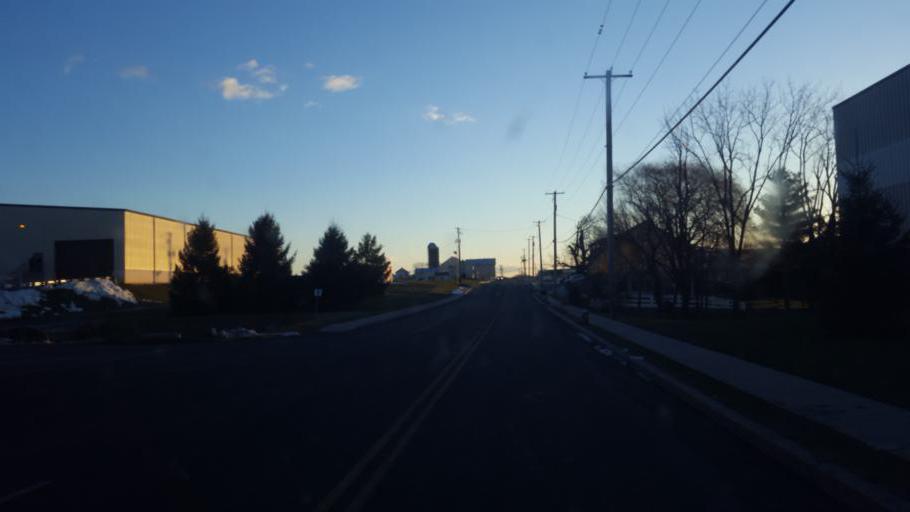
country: US
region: Pennsylvania
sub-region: Lancaster County
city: New Holland
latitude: 40.0905
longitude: -76.0971
